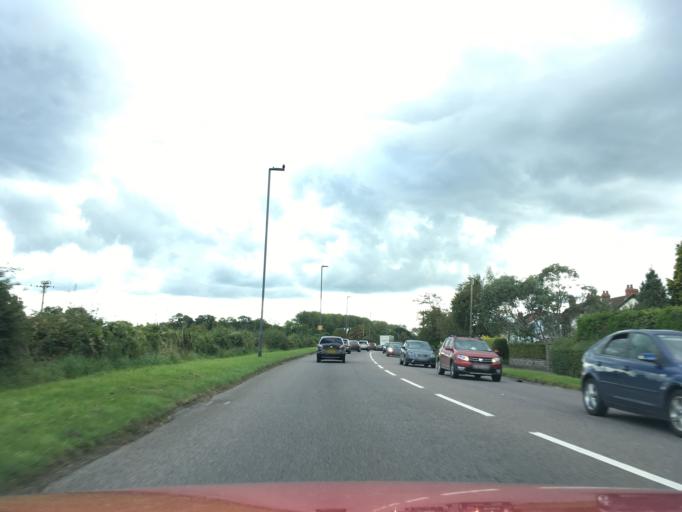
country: GB
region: England
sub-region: South Gloucestershire
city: Alveston
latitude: 51.5883
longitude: -2.5277
